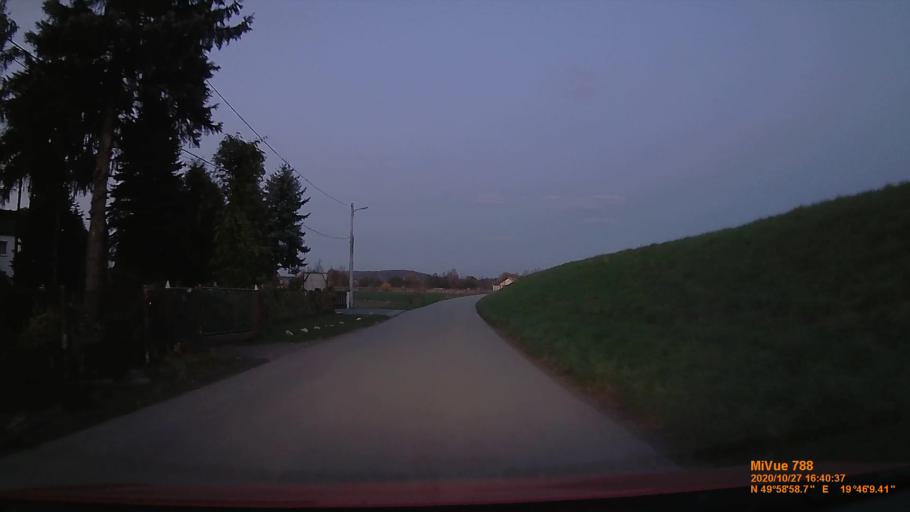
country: PL
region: Lesser Poland Voivodeship
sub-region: Powiat krakowski
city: Raczna
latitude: 49.9831
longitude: 19.7694
